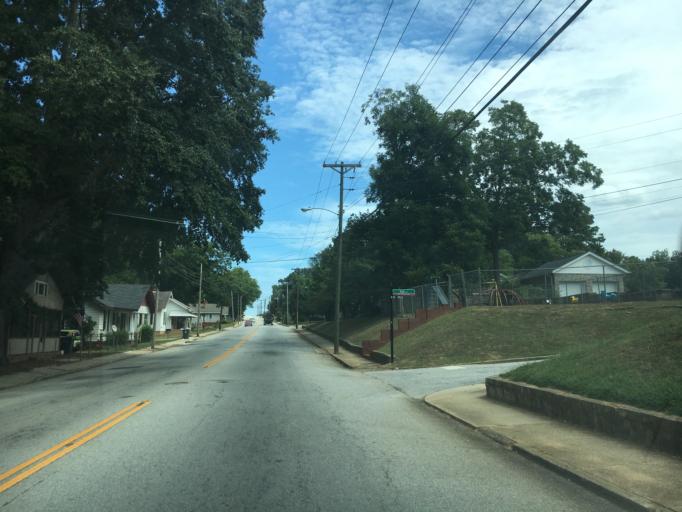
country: US
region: South Carolina
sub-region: Laurens County
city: Laurens
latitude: 34.5043
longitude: -82.0022
